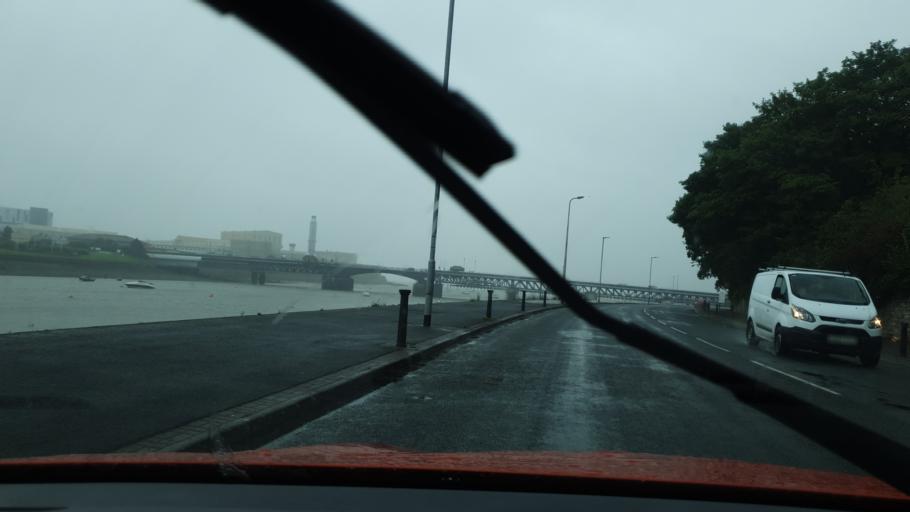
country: GB
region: England
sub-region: Cumbria
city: Barrow in Furness
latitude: 54.1106
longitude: -3.2460
